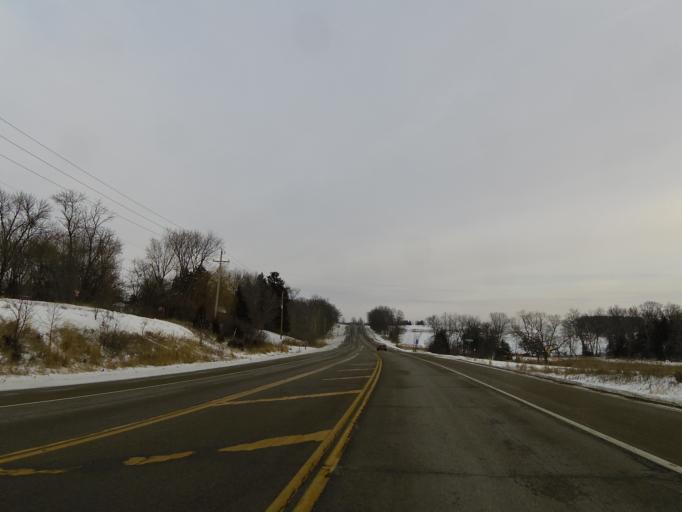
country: US
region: Minnesota
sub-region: Hennepin County
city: Saint Bonifacius
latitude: 44.8990
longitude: -93.7281
